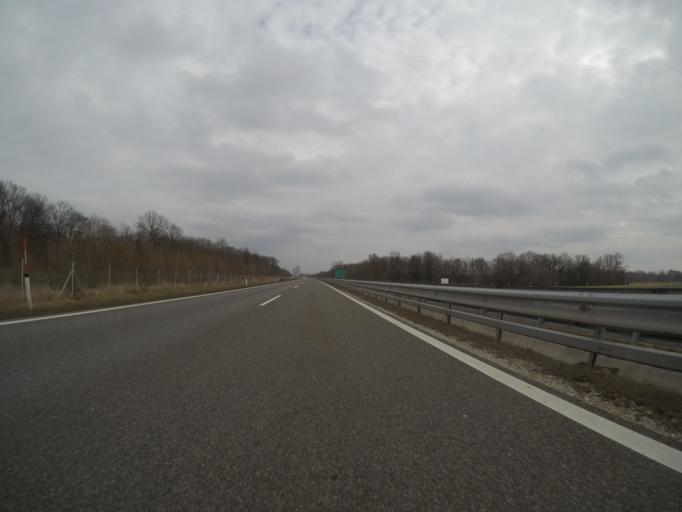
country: SI
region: Turnisce
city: Turnisce
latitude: 46.6074
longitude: 16.3237
